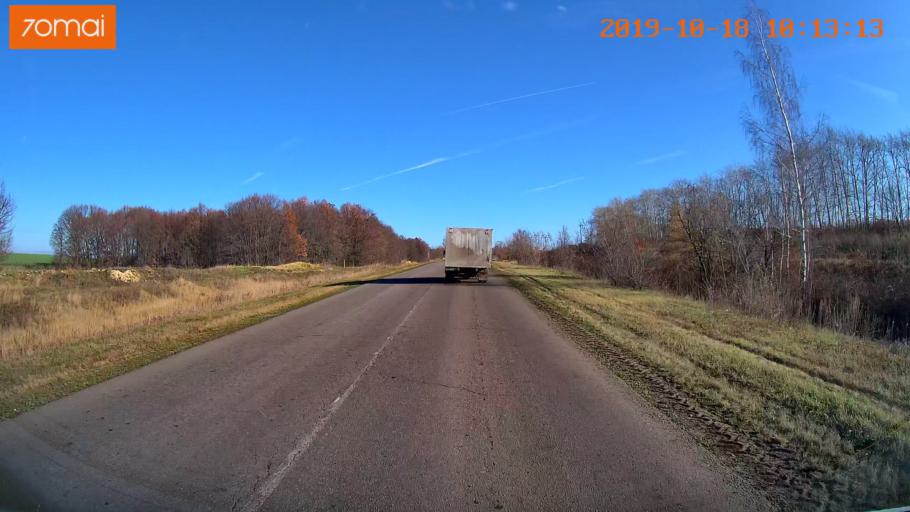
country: RU
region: Tula
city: Kurkino
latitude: 53.4001
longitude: 38.5184
